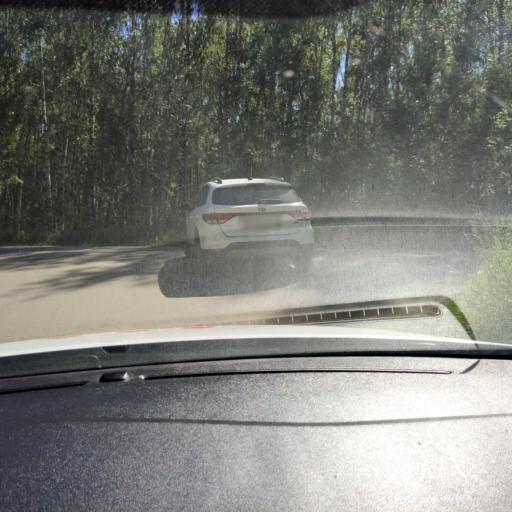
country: RU
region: Tatarstan
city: Staroye Arakchino
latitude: 55.8899
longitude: 49.0321
